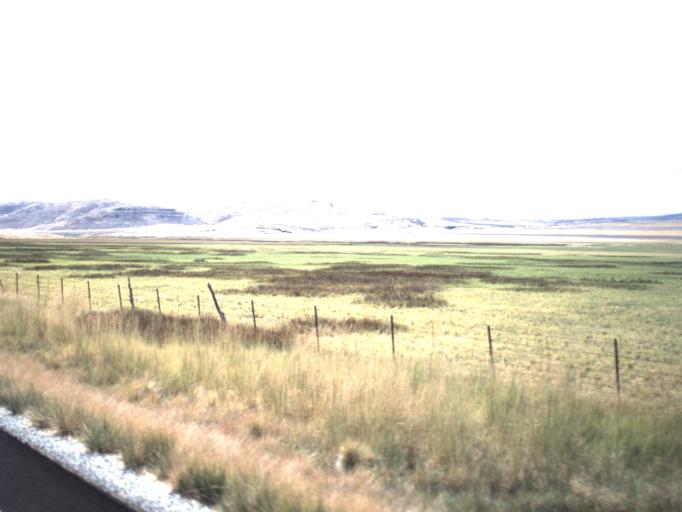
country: US
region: Utah
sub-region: Box Elder County
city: Tremonton
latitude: 41.7418
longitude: -112.4343
